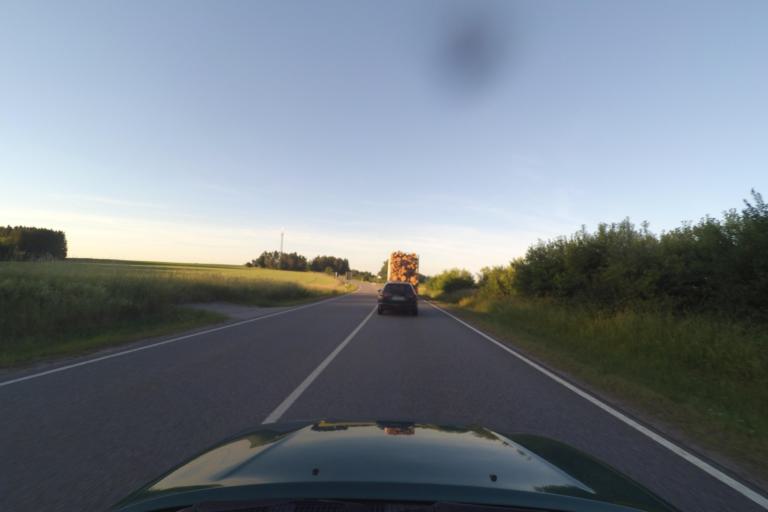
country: DE
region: Bavaria
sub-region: Upper Palatinate
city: Puchersreuth
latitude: 49.8086
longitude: 12.2421
